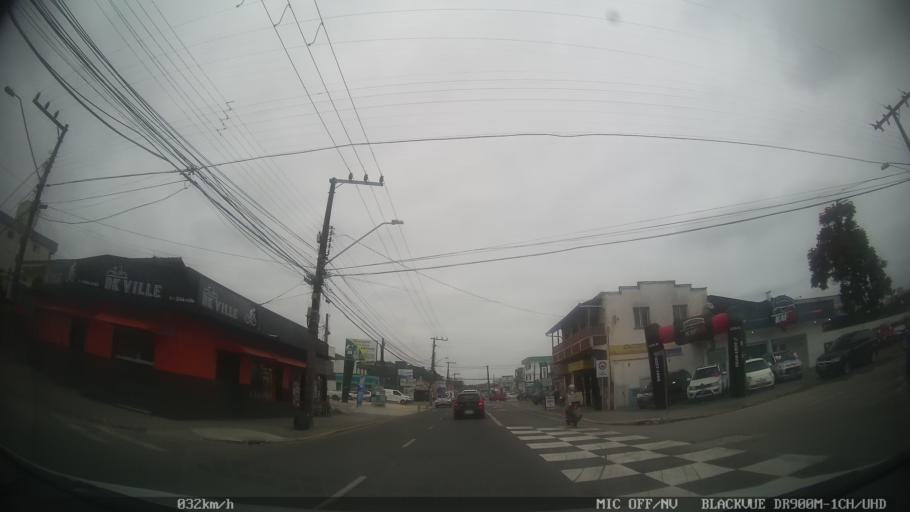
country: BR
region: Santa Catarina
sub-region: Joinville
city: Joinville
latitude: -26.3368
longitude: -48.8475
